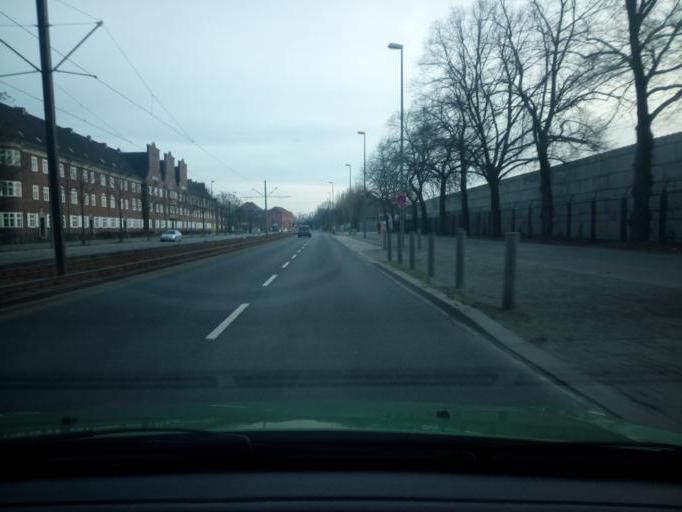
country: DE
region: Berlin
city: Rummelsburg
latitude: 52.4851
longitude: 13.4988
